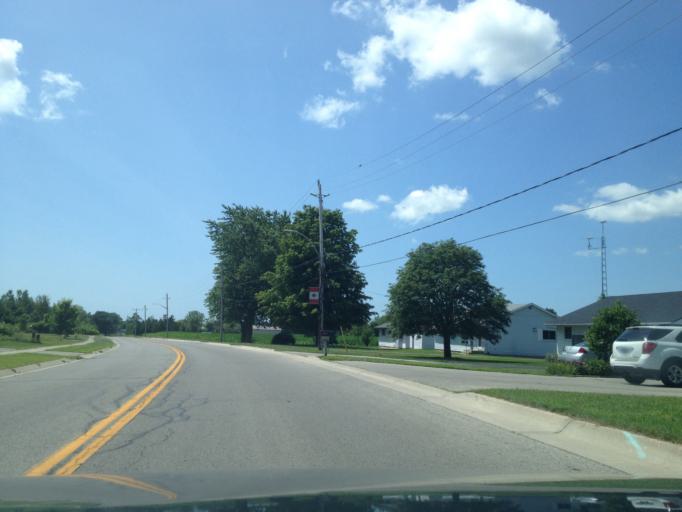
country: CA
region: Ontario
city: Norfolk County
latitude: 42.6185
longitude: -80.4577
